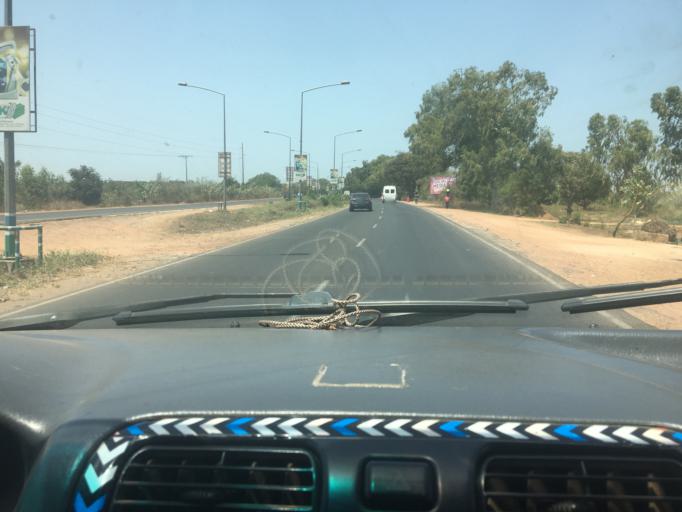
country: GM
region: Banjul
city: Bakau
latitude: 13.4694
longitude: -16.6371
